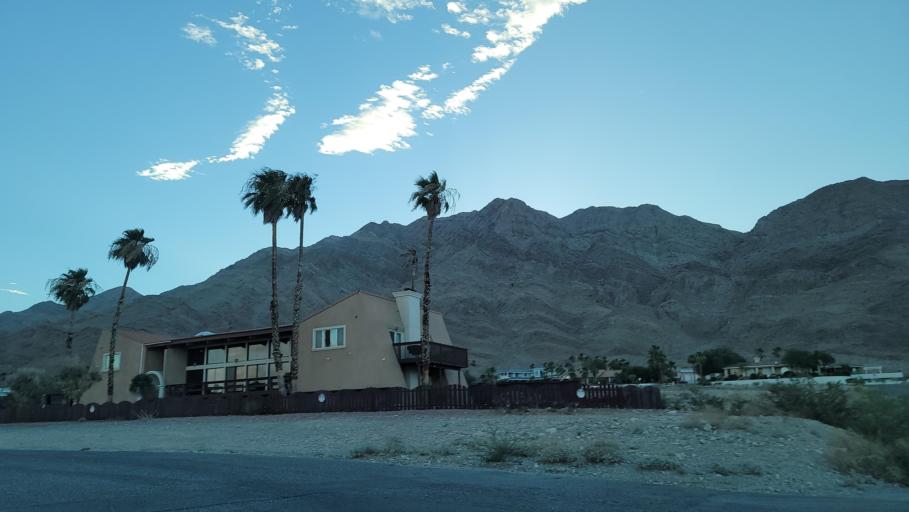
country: US
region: Nevada
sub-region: Clark County
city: Sunrise Manor
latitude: 36.1665
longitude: -115.0170
